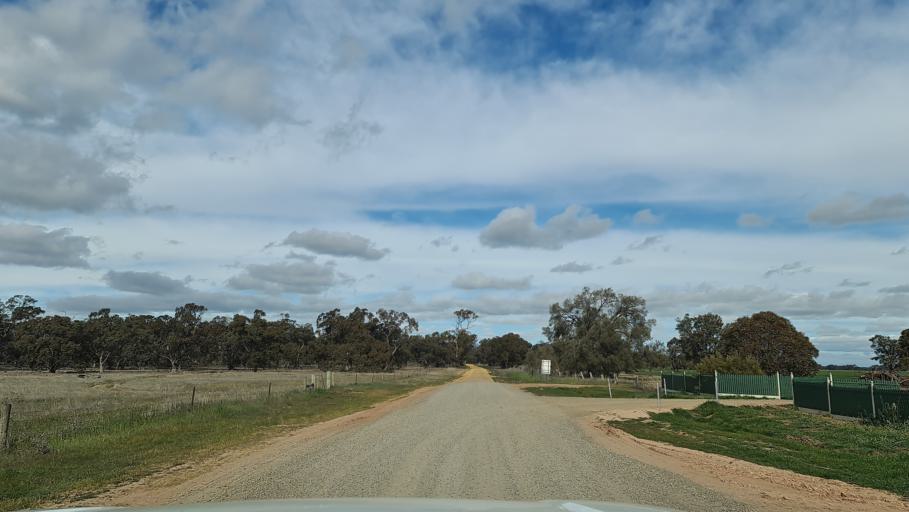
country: AU
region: Victoria
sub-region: Horsham
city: Horsham
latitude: -36.6318
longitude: 142.4117
